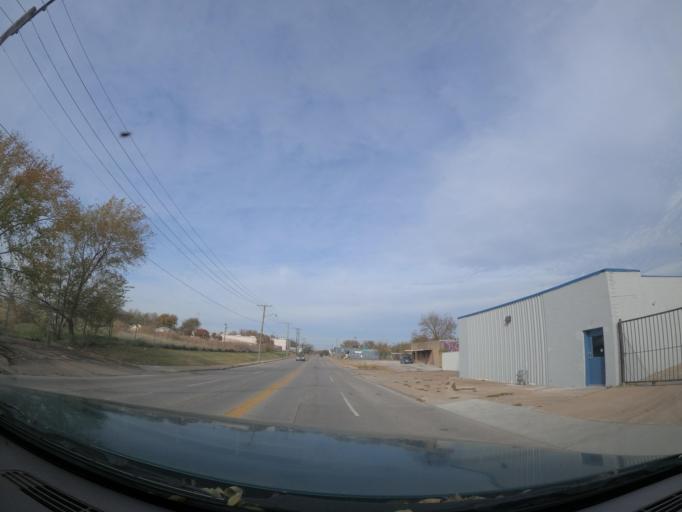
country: US
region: Oklahoma
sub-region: Tulsa County
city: Tulsa
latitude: 36.1709
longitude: -95.9671
